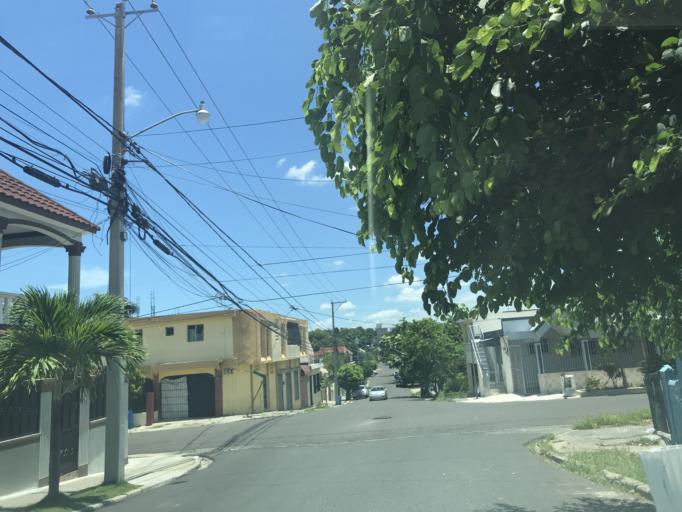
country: DO
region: Santiago
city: Santiago de los Caballeros
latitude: 19.4409
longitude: -70.6967
